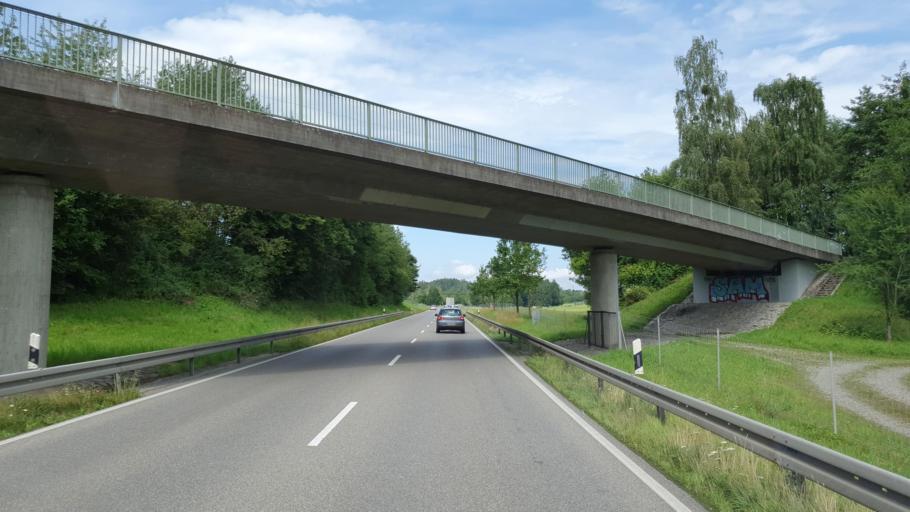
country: DE
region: Bavaria
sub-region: Swabia
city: Bodolz
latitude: 47.5860
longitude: 9.6587
